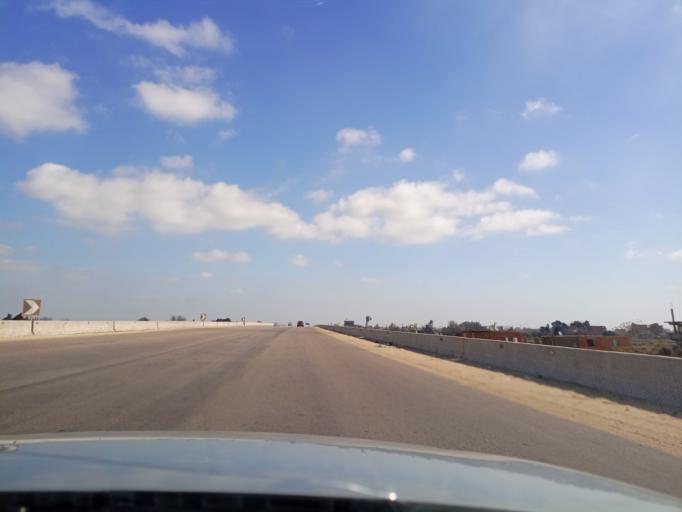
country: EG
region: Muhafazat al Minufiyah
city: Al Bajur
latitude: 30.3935
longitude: 31.0021
